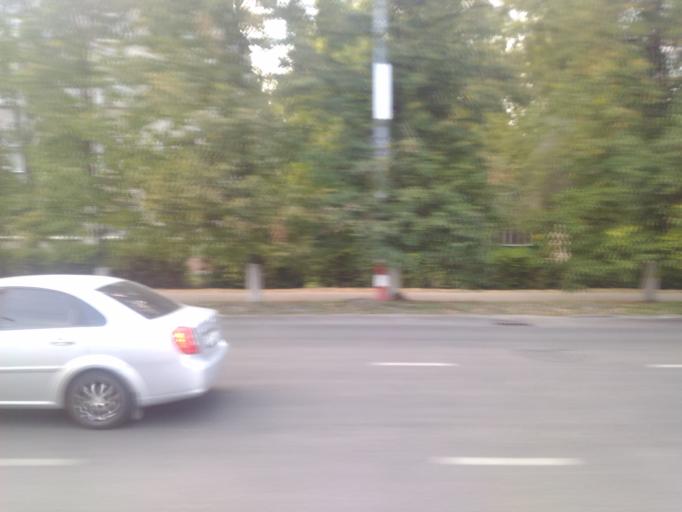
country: RU
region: Ulyanovsk
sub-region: Ulyanovskiy Rayon
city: Ulyanovsk
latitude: 54.2914
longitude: 48.3101
